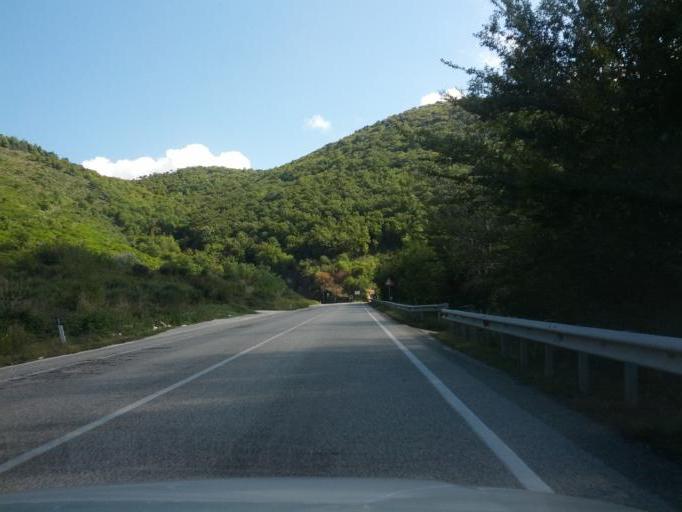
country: IT
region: Campania
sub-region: Provincia di Caserta
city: Mignano Monte Lungo
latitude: 41.4422
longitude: 13.9991
